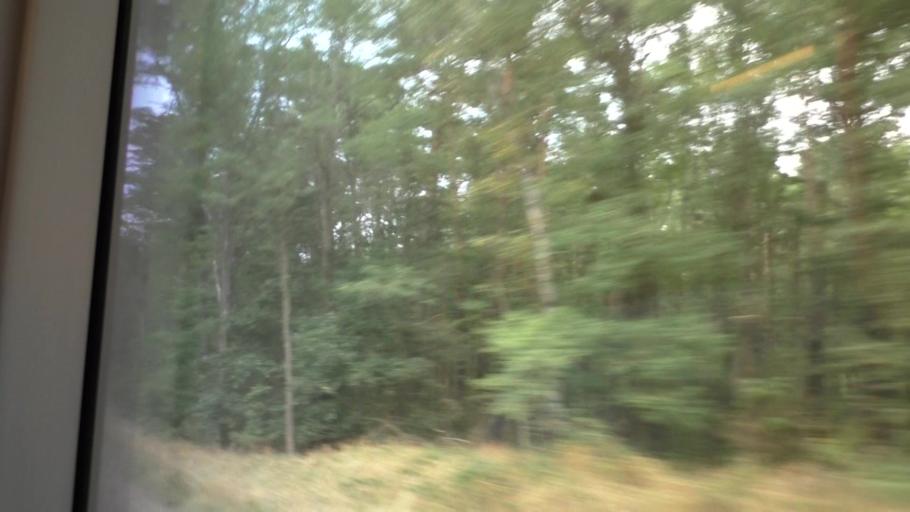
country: DE
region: Brandenburg
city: Mullrose
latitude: 52.2238
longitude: 14.4272
